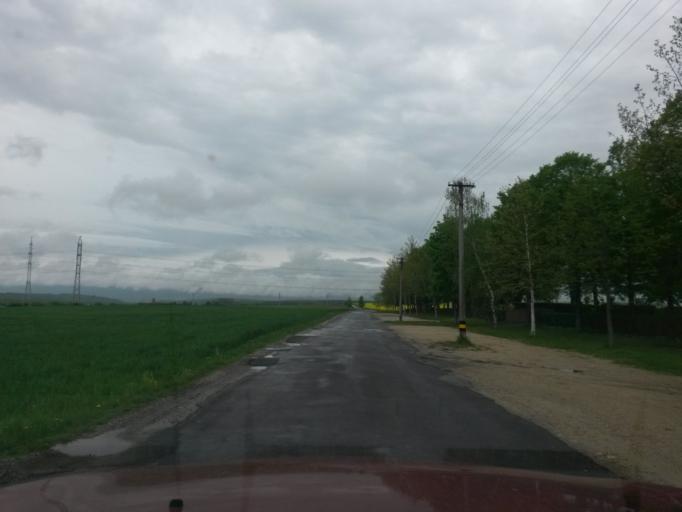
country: SK
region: Kosicky
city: Moldava nad Bodvou
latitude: 48.6012
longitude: 21.0204
